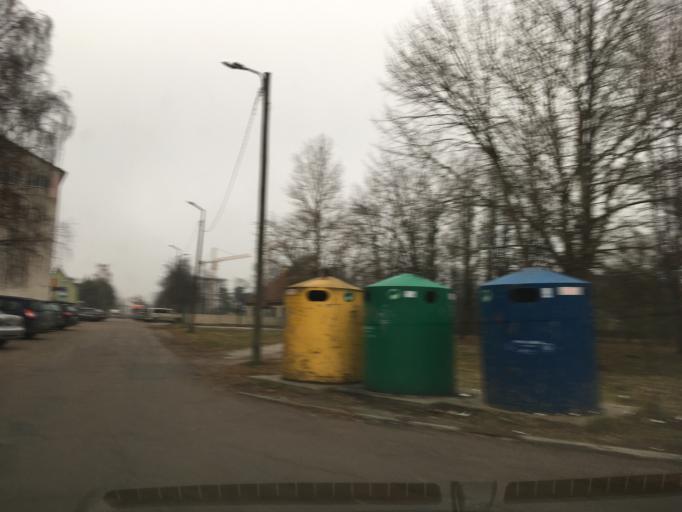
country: EE
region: Harju
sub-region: Tallinna linn
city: Tallinn
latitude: 59.3995
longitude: 24.7226
